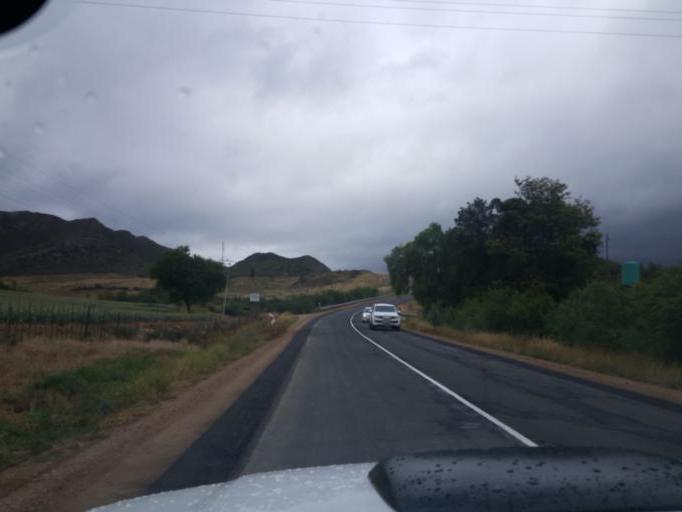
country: ZA
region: Western Cape
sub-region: Eden District Municipality
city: Oudtshoorn
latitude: -33.4068
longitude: 22.2255
